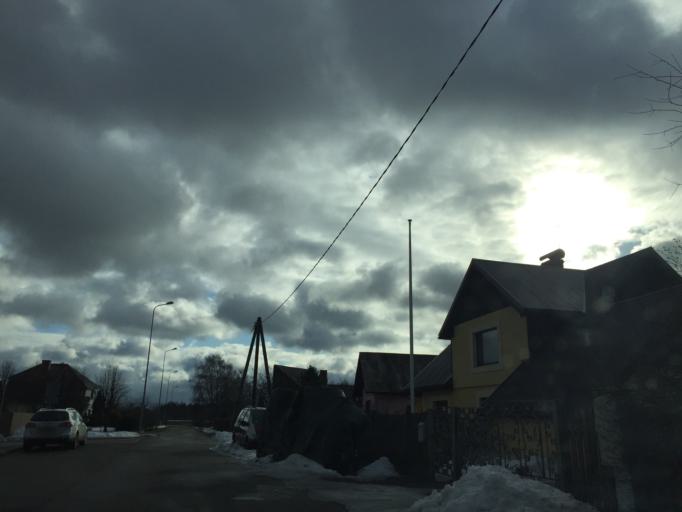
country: LV
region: Aloja
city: Aloja
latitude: 57.7712
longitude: 24.8186
